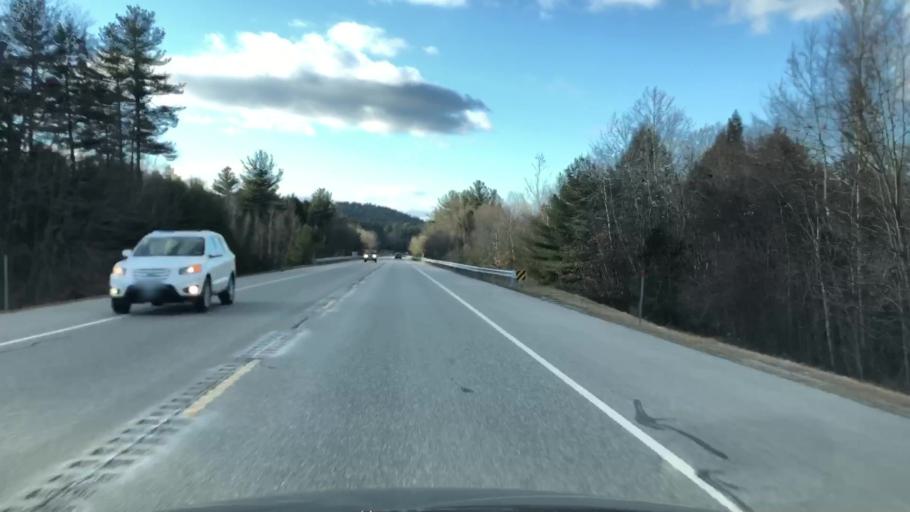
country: US
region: New Hampshire
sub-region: Hillsborough County
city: Milford
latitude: 42.8338
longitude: -71.6911
